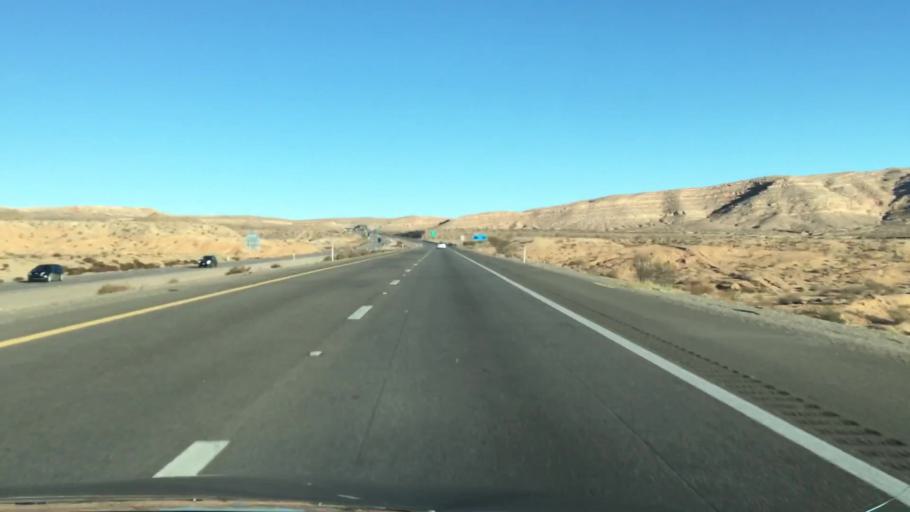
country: US
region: Nevada
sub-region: Clark County
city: Moapa Town
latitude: 36.6668
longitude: -114.5427
